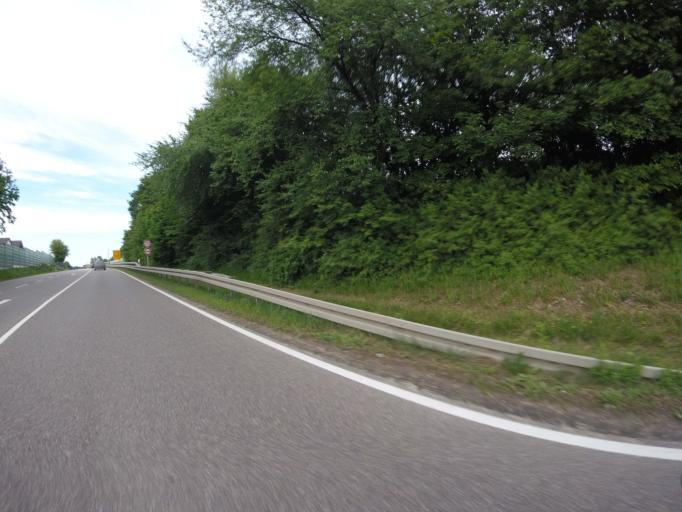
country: DE
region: Bavaria
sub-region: Upper Bavaria
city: Ilmmunster
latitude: 48.4843
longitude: 11.5108
